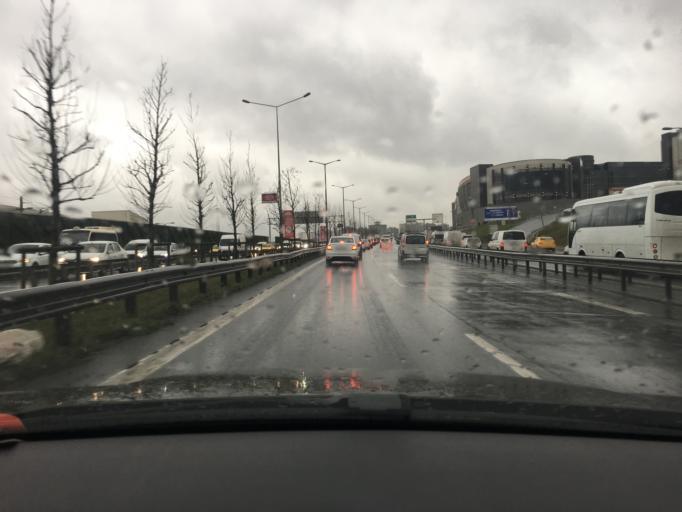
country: TR
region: Istanbul
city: Esenler
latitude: 41.0389
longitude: 28.8878
